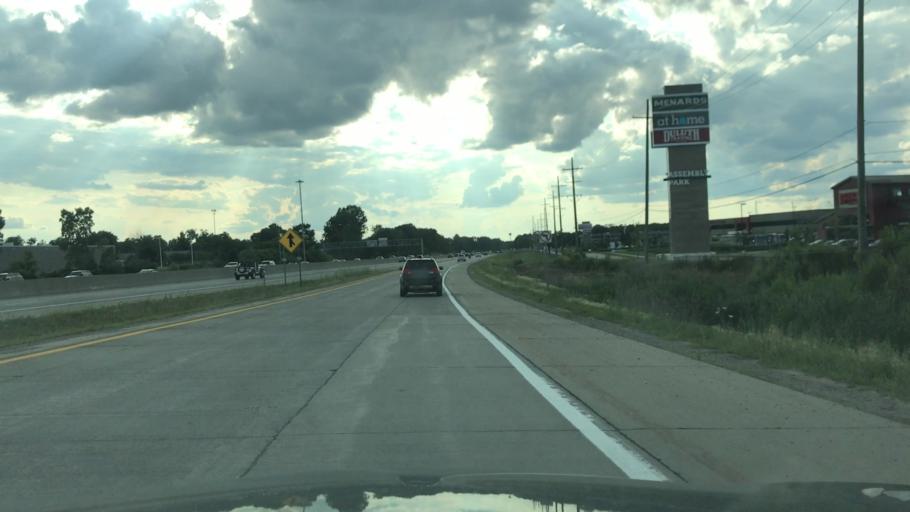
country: US
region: Michigan
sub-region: Oakland County
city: Wixom
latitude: 42.4989
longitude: -83.5388
